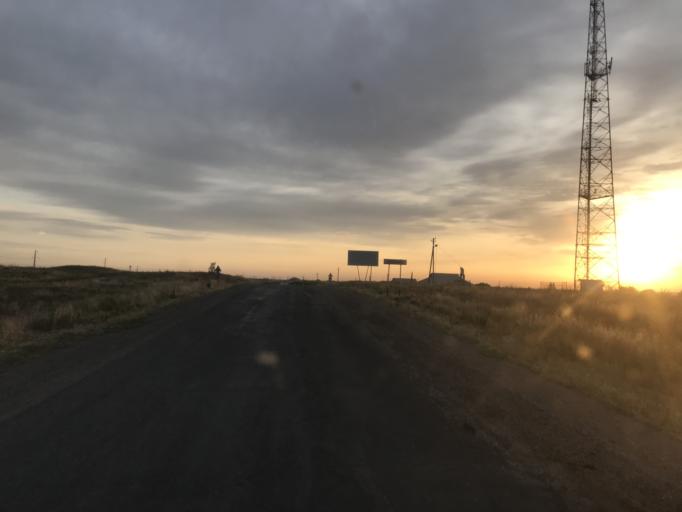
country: UZ
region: Toshkent
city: Amir Timur
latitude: 41.2279
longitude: 68.8063
